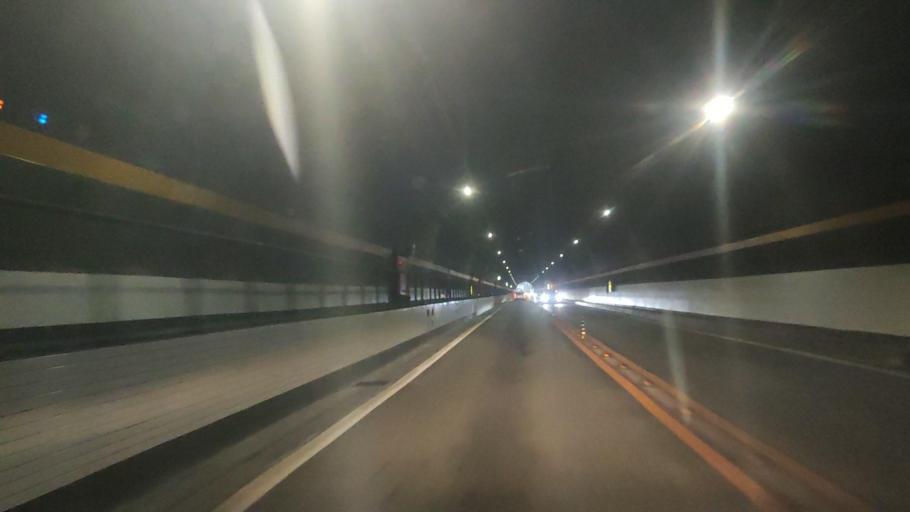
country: JP
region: Nagasaki
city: Nagasaki-shi
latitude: 32.7749
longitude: 129.8887
